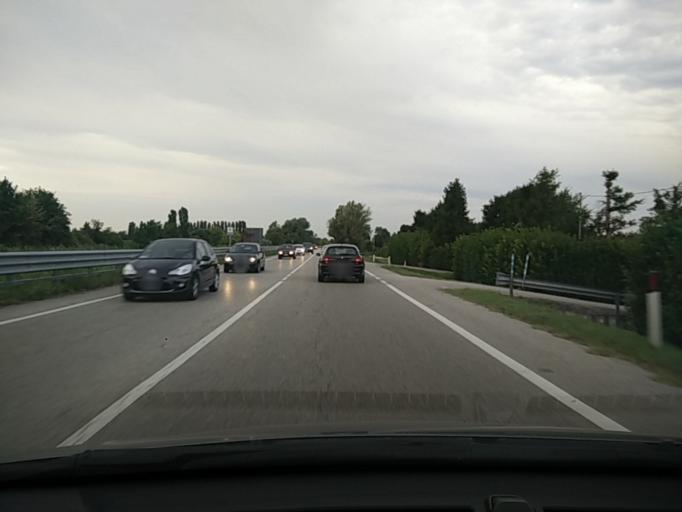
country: IT
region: Veneto
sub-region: Provincia di Venezia
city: Passarella
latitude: 45.5618
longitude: 12.5722
